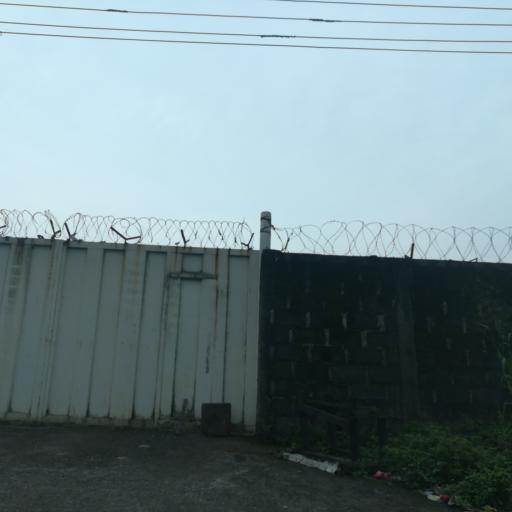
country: NG
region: Rivers
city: Port Harcourt
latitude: 4.7646
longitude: 7.0116
